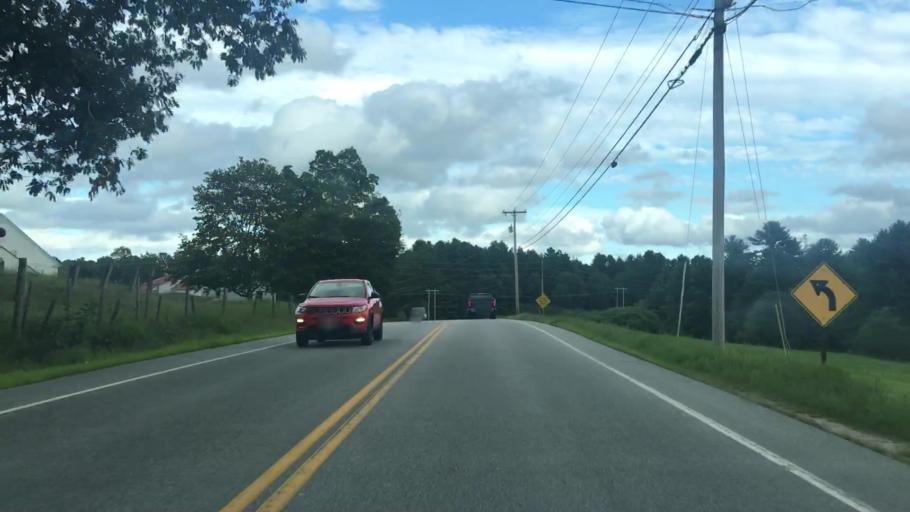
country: US
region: Maine
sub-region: York County
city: Dayton
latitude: 43.5431
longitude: -70.5248
